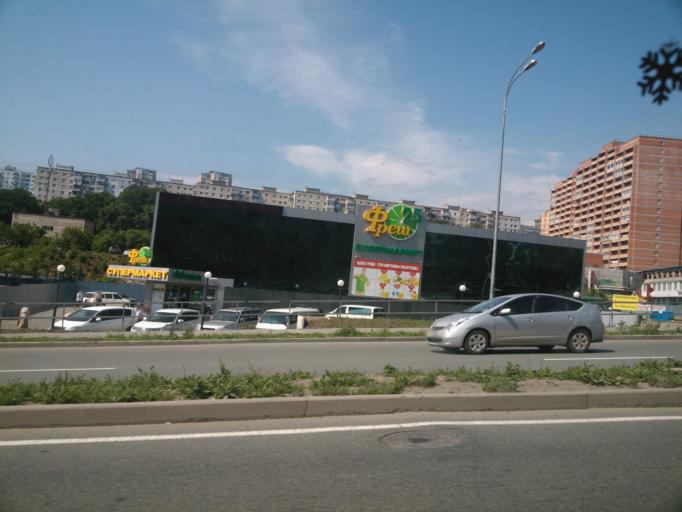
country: RU
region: Primorskiy
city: Vladivostok
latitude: 43.0930
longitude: 131.9093
